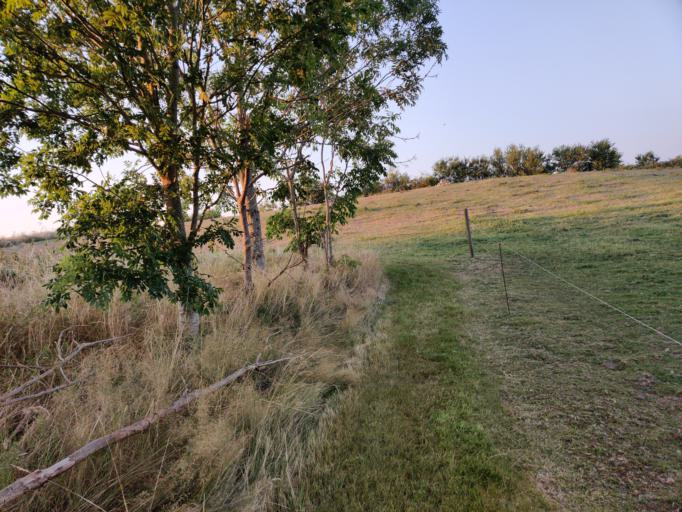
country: DK
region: South Denmark
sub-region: AEro Kommune
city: AEroskobing
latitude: 54.8983
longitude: 10.3120
